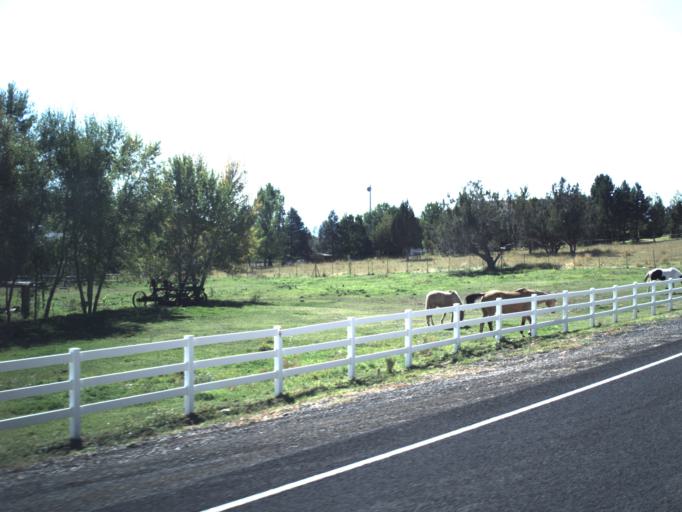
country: US
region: Utah
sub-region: Beaver County
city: Beaver
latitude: 38.2822
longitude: -112.5922
